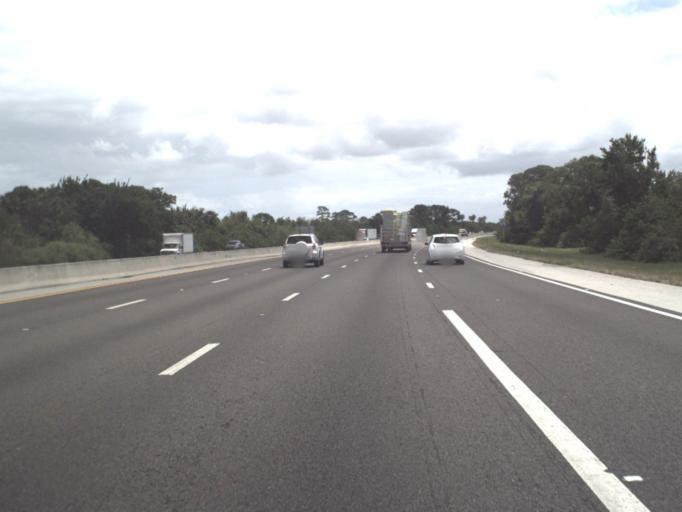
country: US
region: Florida
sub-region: Brevard County
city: Rockledge
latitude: 28.2878
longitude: -80.7370
